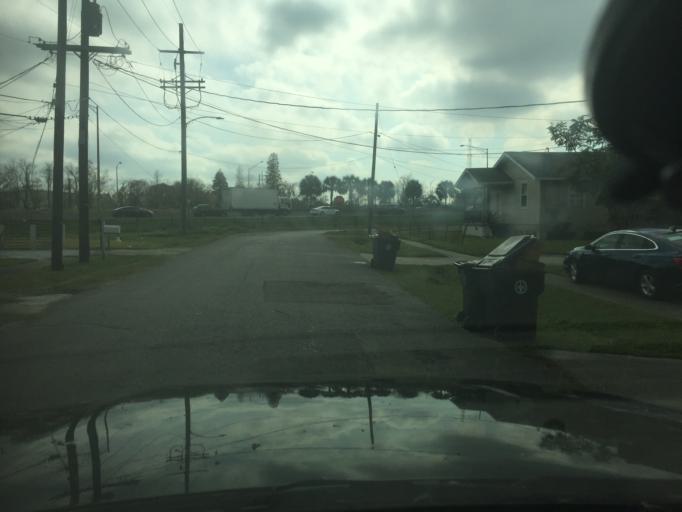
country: US
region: Louisiana
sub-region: Orleans Parish
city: New Orleans
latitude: 30.0012
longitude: -90.0411
